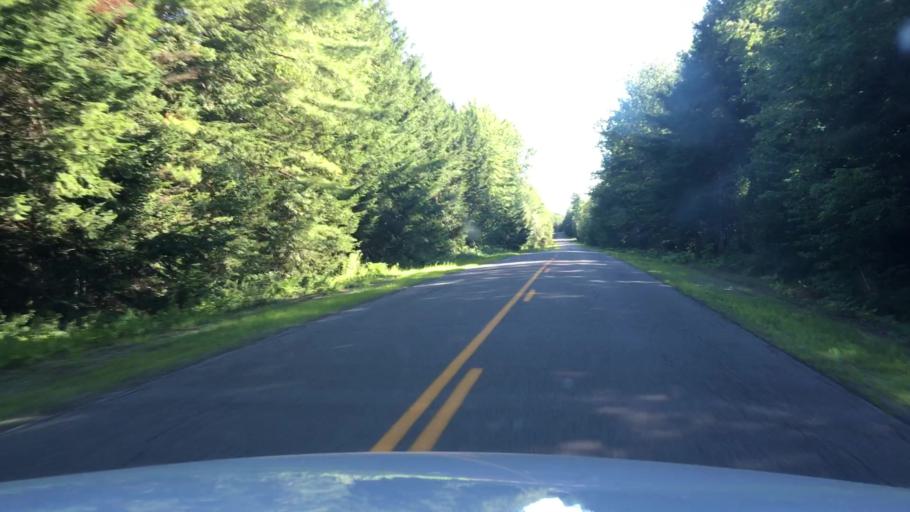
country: US
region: Maine
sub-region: Penobscot County
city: Enfield
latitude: 45.2189
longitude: -68.5825
